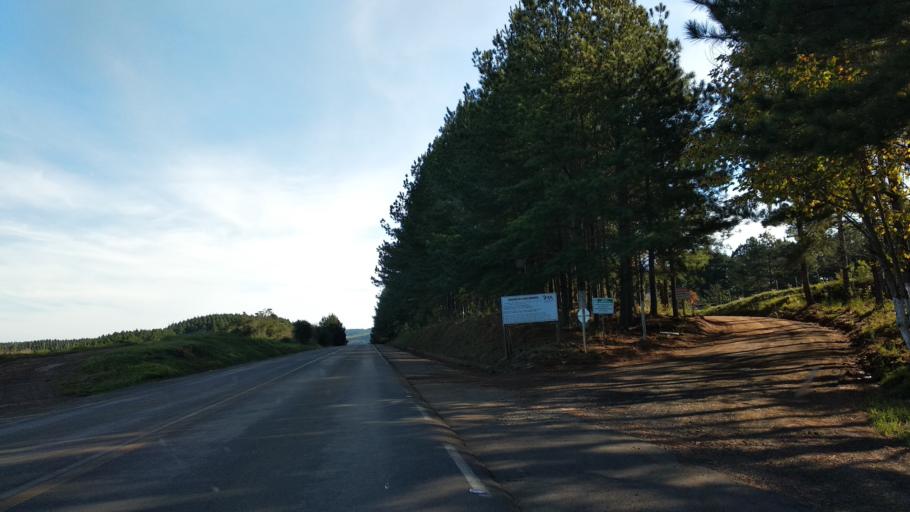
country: BR
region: Santa Catarina
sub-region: Celso Ramos
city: Celso Ramos
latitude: -27.5432
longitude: -51.4212
